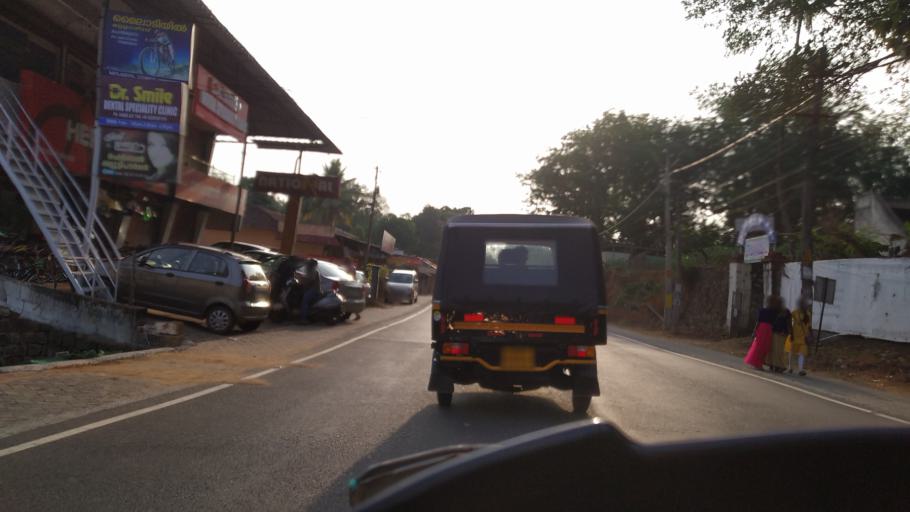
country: IN
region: Kerala
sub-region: Kottayam
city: Erattupetta
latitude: 9.5662
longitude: 76.7528
